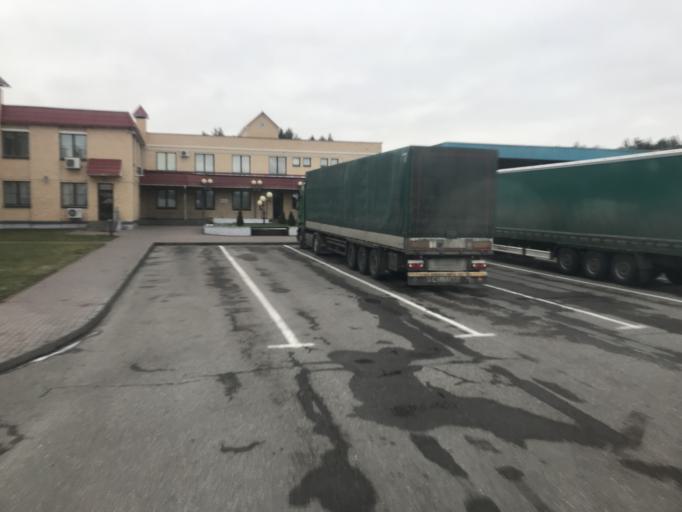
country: BY
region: Grodnenskaya
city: Vyalikaya Byerastavitsa
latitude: 53.1219
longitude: 23.8973
